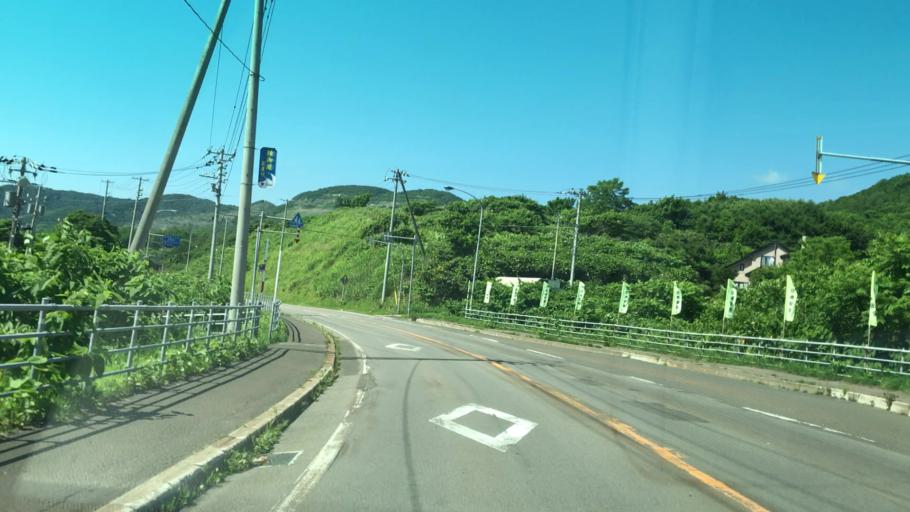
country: JP
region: Hokkaido
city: Iwanai
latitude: 43.0638
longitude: 140.4984
